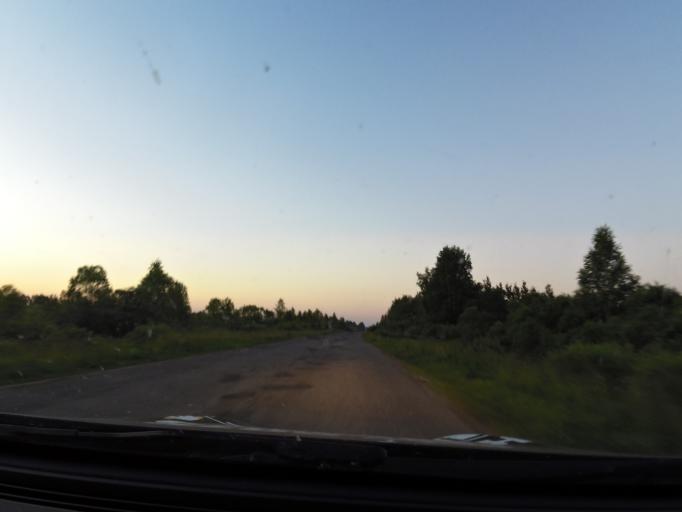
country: RU
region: Kostroma
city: Buy
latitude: 58.4733
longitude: 41.4284
